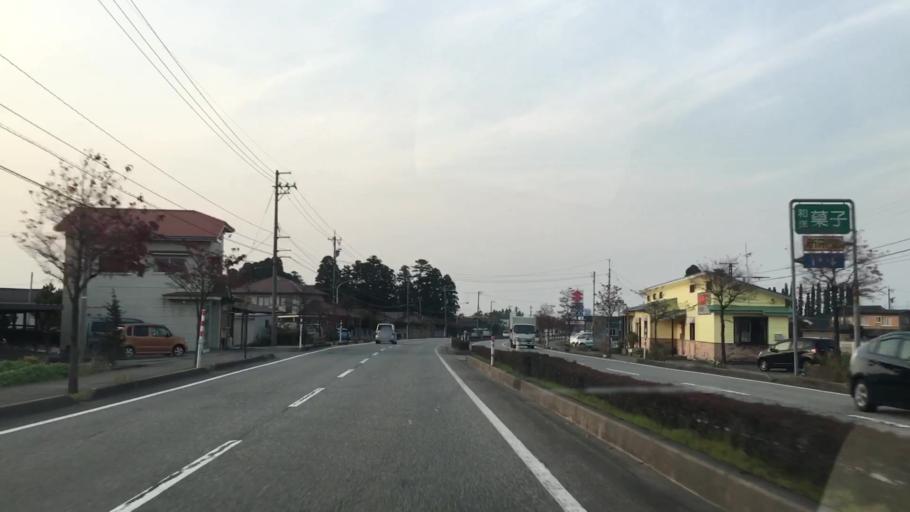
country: JP
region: Toyama
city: Toyama-shi
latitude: 36.6407
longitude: 137.2376
